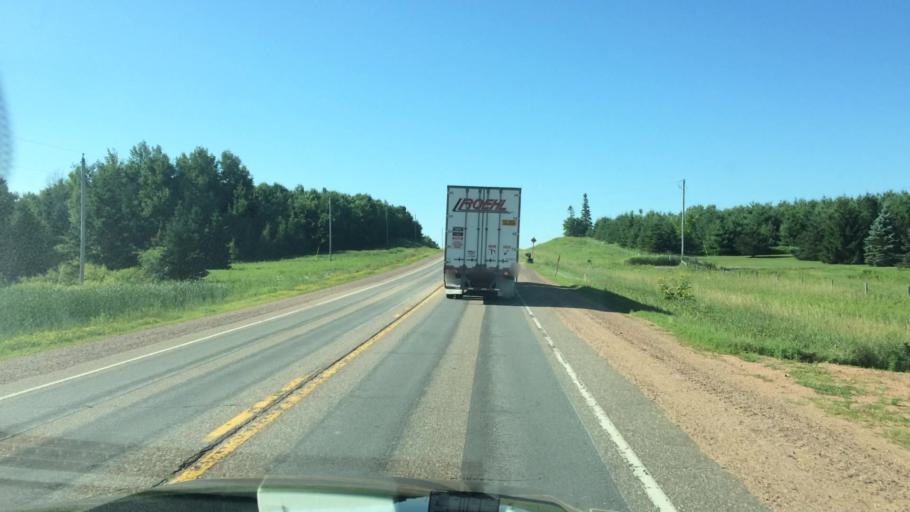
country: US
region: Wisconsin
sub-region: Marathon County
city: Athens
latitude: 44.9277
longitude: -90.0788
